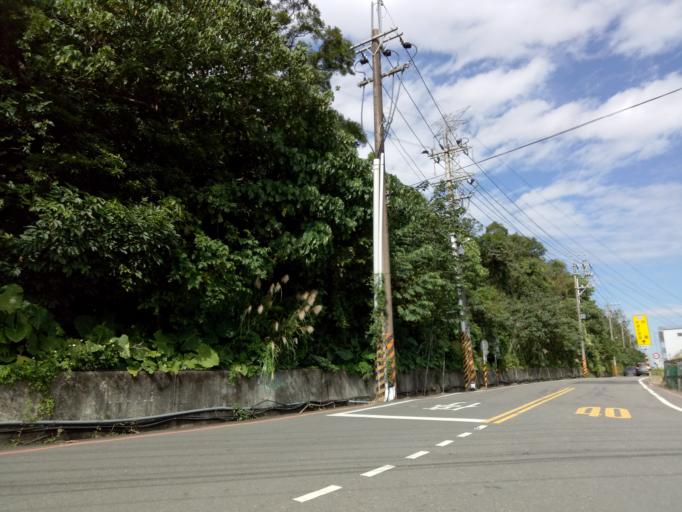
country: TW
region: Taiwan
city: Daxi
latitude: 24.8951
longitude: 121.2856
